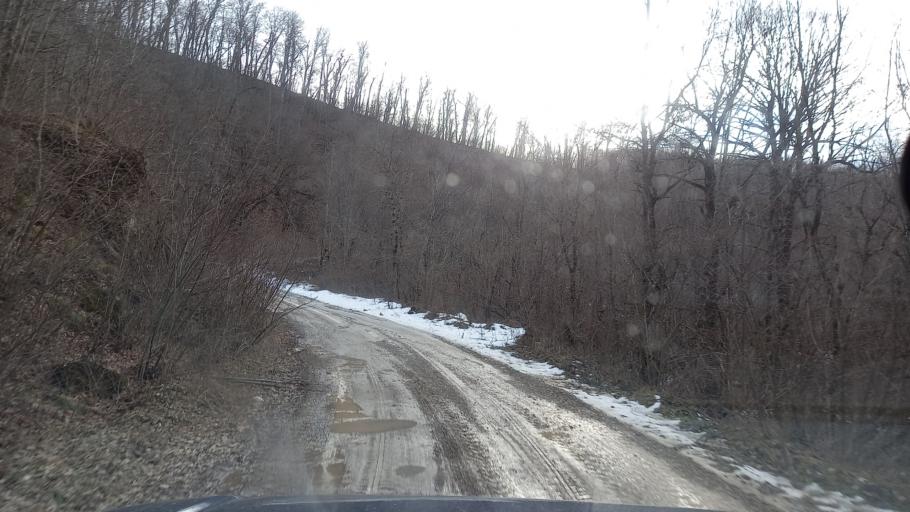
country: RU
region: Adygeya
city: Kamennomostskiy
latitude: 44.1524
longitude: 40.2981
